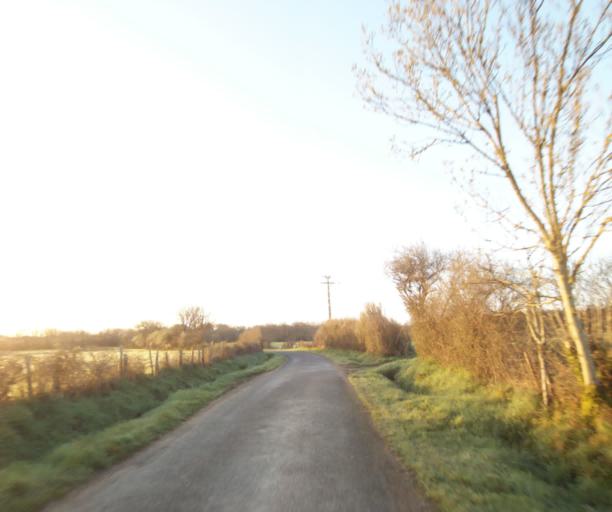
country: FR
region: Pays de la Loire
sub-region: Departement de la Loire-Atlantique
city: Bouvron
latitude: 47.4334
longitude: -1.8898
